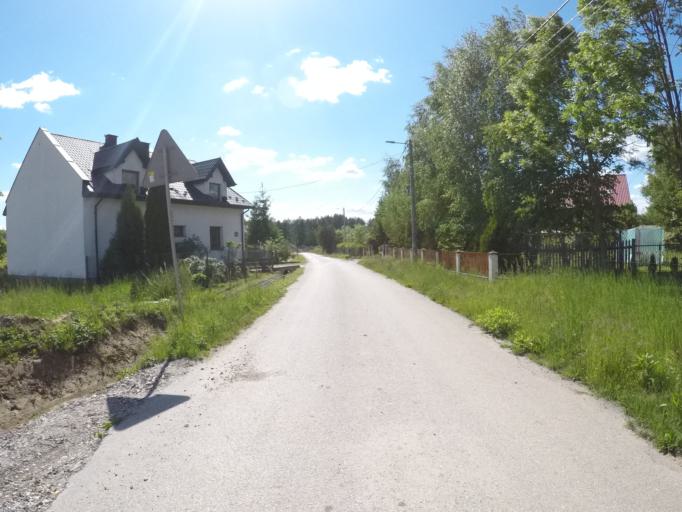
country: PL
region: Swietokrzyskie
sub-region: Powiat kielecki
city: Miedziana Gora
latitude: 50.9236
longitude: 20.5350
